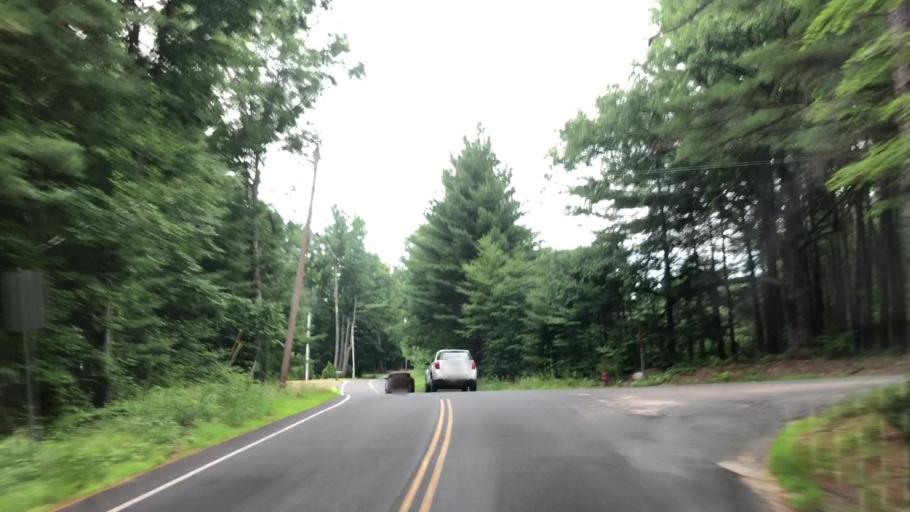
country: US
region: Massachusetts
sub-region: Hampshire County
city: Southampton
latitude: 42.1971
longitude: -72.7442
